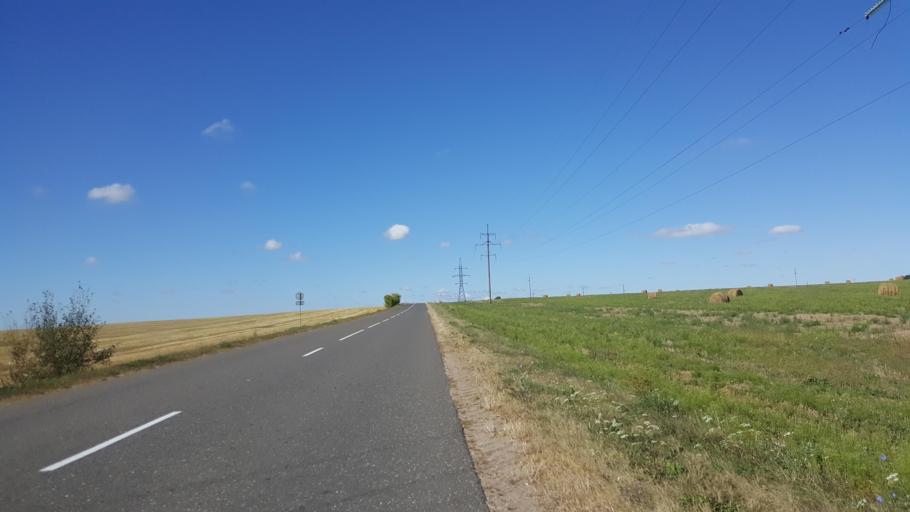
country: BY
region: Brest
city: Kamyanyets
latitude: 52.3799
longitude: 23.6782
